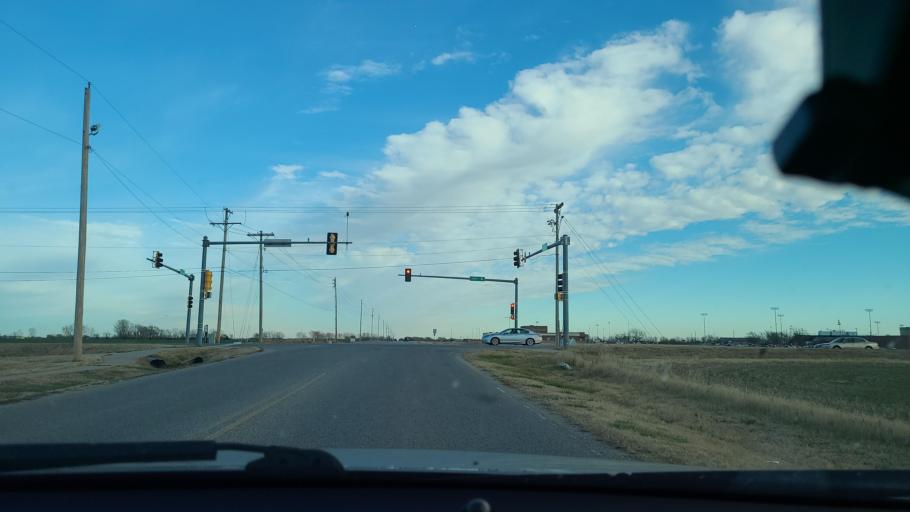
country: US
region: Kansas
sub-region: Sedgwick County
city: Goddard
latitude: 37.6496
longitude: -97.5718
